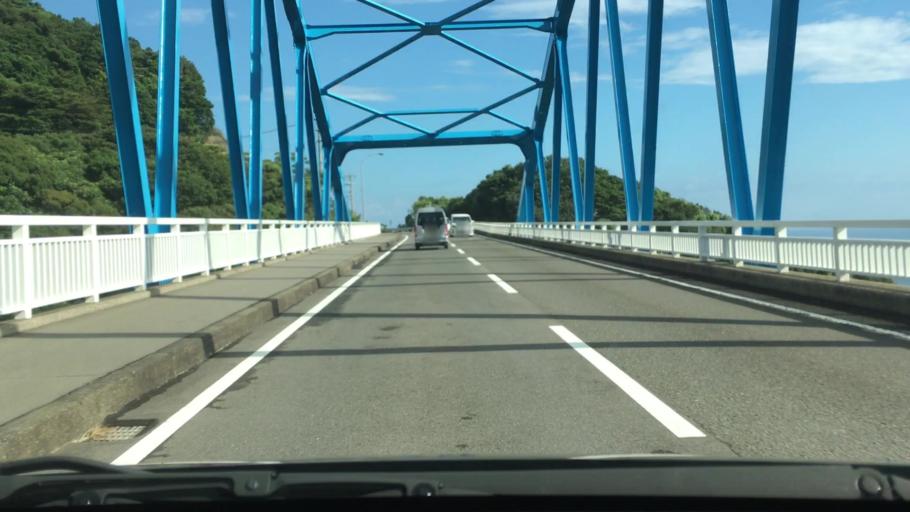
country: JP
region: Nagasaki
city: Togitsu
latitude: 32.8509
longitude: 129.6904
